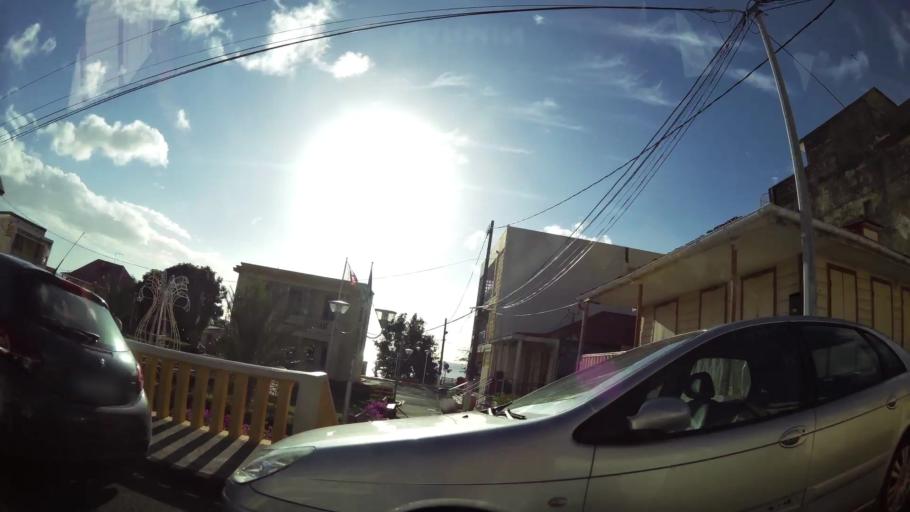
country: GP
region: Guadeloupe
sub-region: Guadeloupe
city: Pointe-Noire
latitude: 16.2328
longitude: -61.7899
